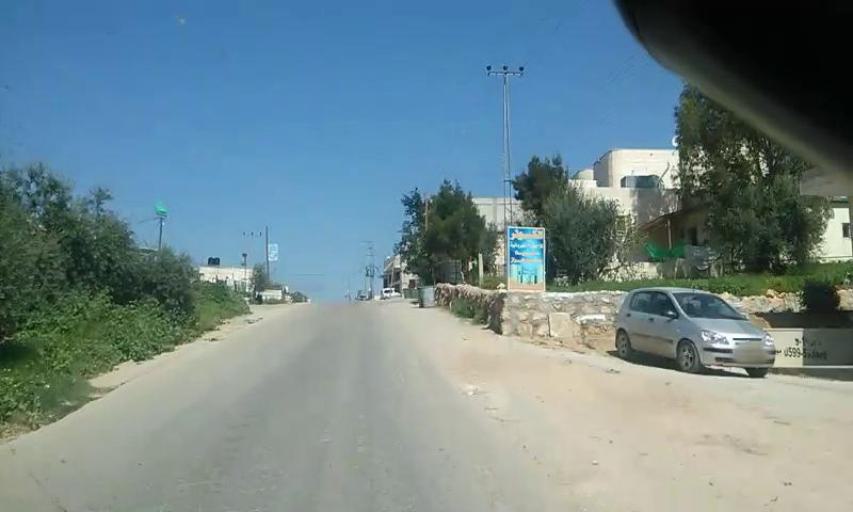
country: PS
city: Dayr Samit
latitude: 31.5040
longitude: 34.9673
